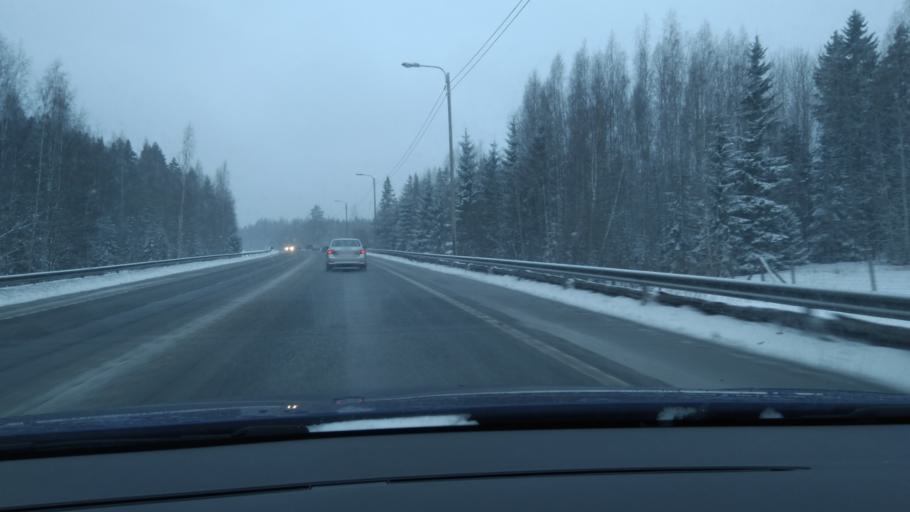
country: FI
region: Pirkanmaa
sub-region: Tampere
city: Tampere
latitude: 61.5185
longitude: 23.9195
